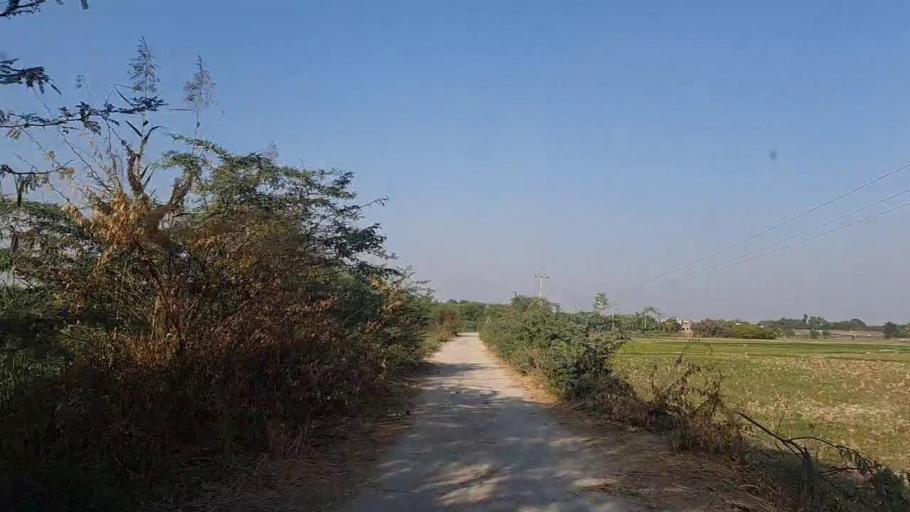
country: PK
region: Sindh
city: Thatta
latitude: 24.7643
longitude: 67.9651
